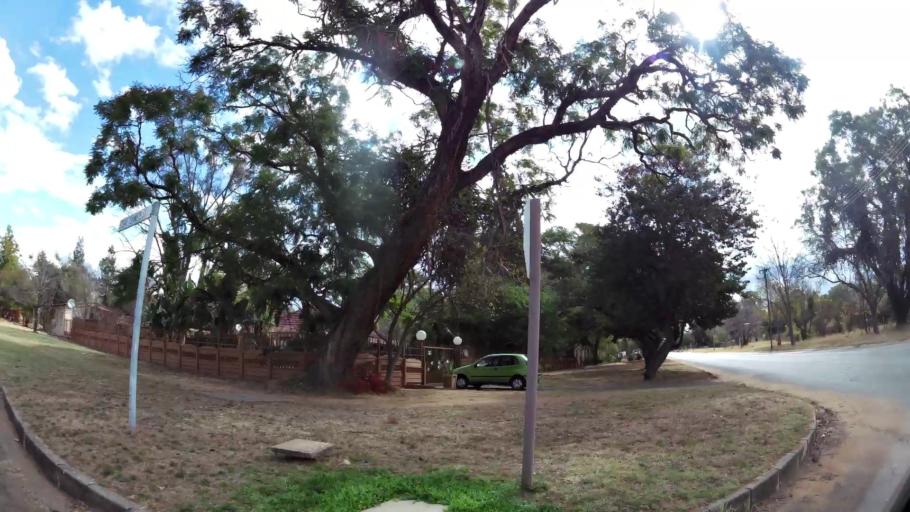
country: ZA
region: Limpopo
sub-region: Waterberg District Municipality
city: Modimolle
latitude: -24.7058
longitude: 28.4073
